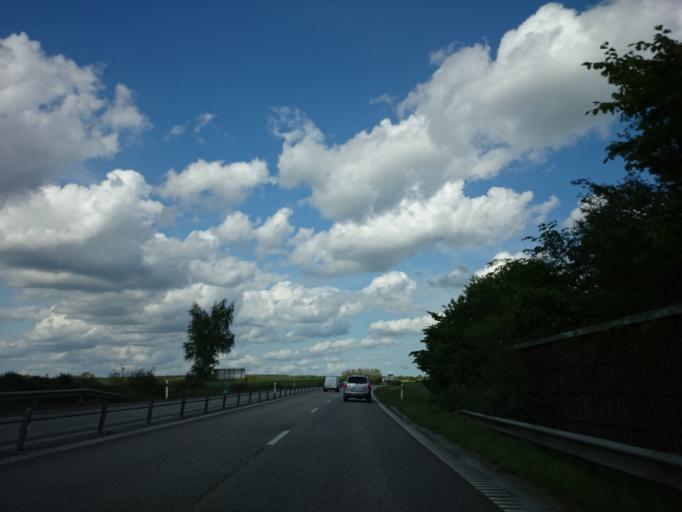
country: SE
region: Skane
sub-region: Horby Kommun
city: Hoerby
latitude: 55.8505
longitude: 13.6056
